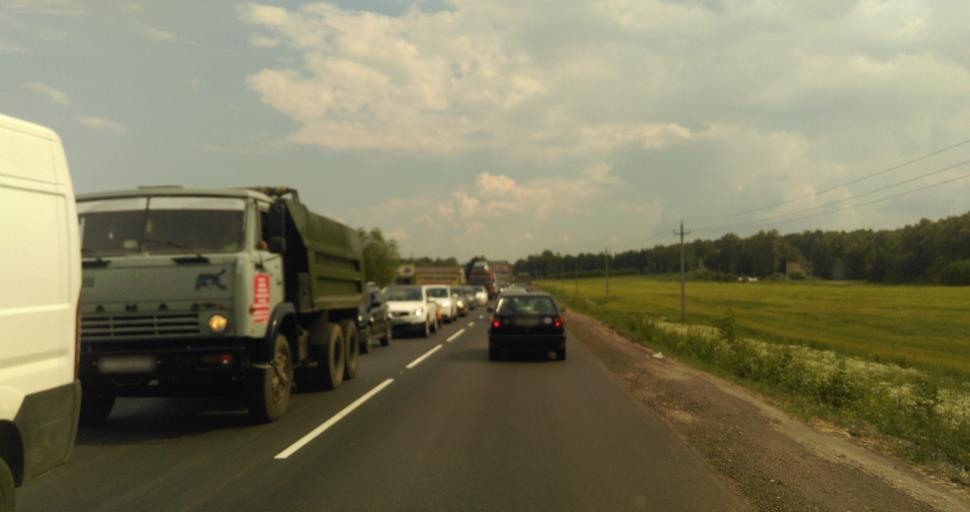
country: RU
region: Moskovskaya
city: Zhitnevo
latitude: 55.3506
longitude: 37.8976
